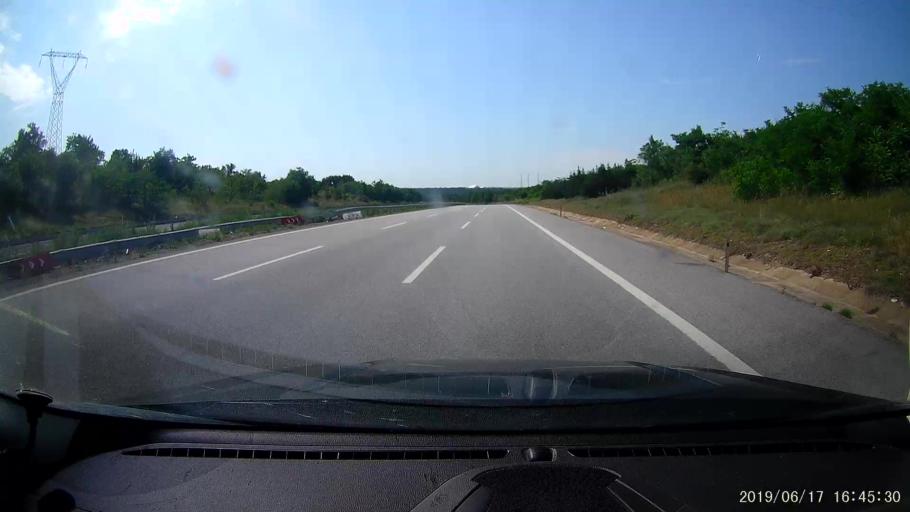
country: TR
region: Kirklareli
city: Babaeski
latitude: 41.4893
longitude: 27.2311
